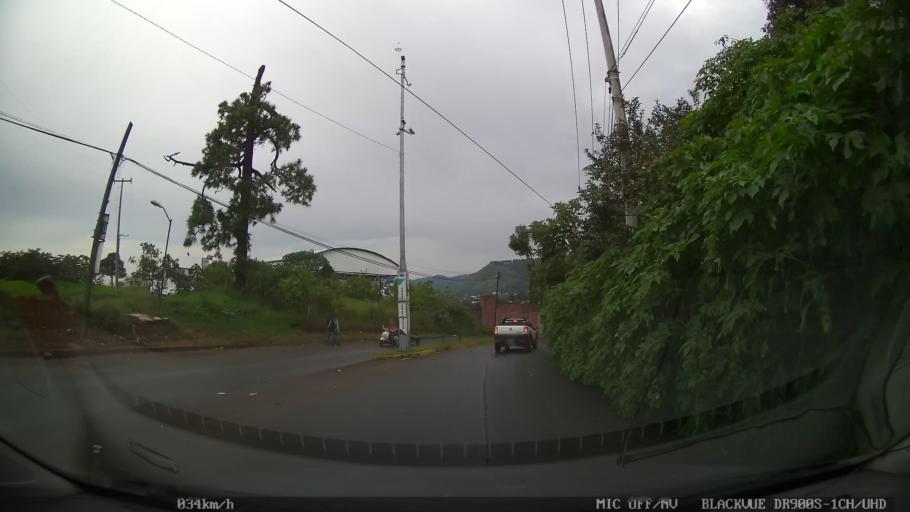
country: MX
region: Michoacan
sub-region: Uruapan
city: Santa Rosa (Santa Barbara)
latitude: 19.3879
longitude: -102.0516
